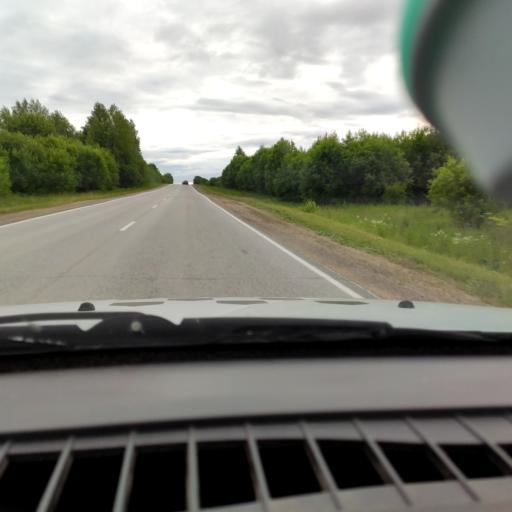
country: RU
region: Perm
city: Lys'va
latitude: 58.1386
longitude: 57.7412
